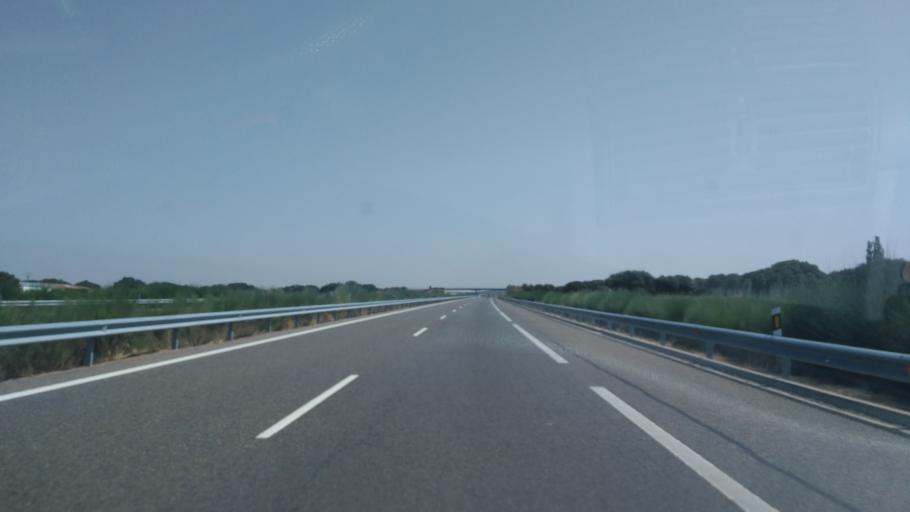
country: ES
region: Castille and Leon
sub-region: Provincia de Salamanca
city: San Munoz
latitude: 40.8060
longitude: -6.1902
